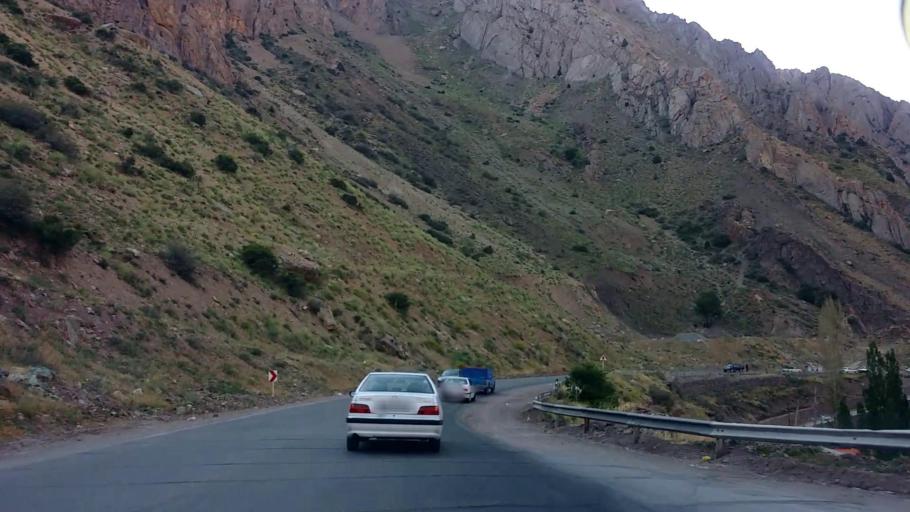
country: IR
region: Tehran
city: Tajrish
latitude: 36.0702
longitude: 51.3097
